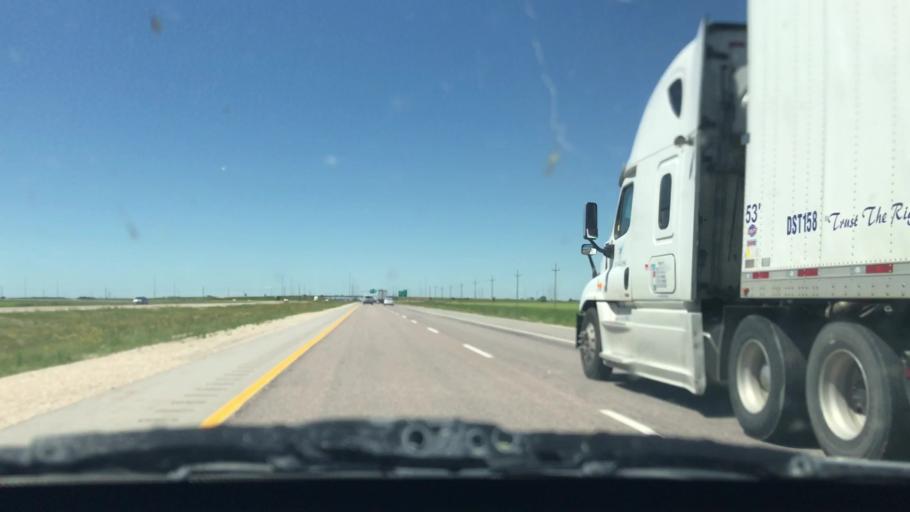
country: CA
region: Manitoba
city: Steinbach
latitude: 49.6948
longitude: -96.6300
